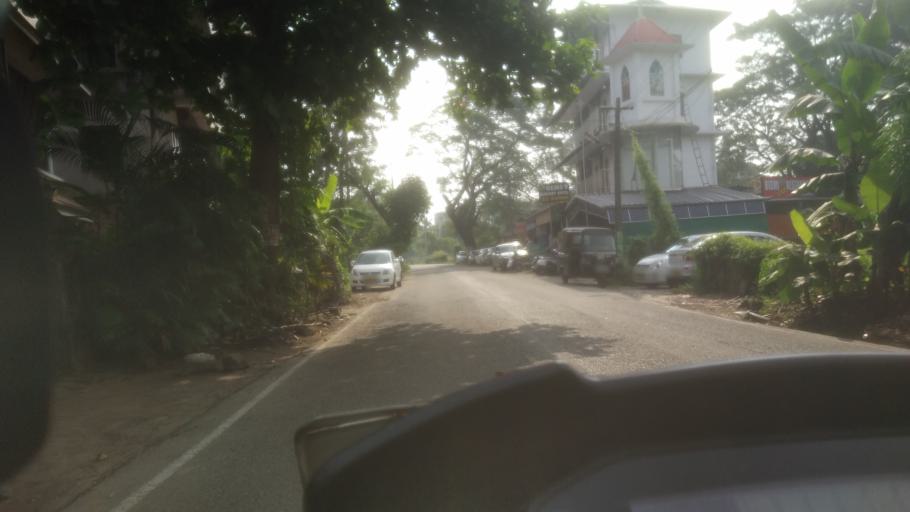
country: IN
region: Kerala
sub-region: Ernakulam
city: Angamali
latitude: 10.1609
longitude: 76.3864
